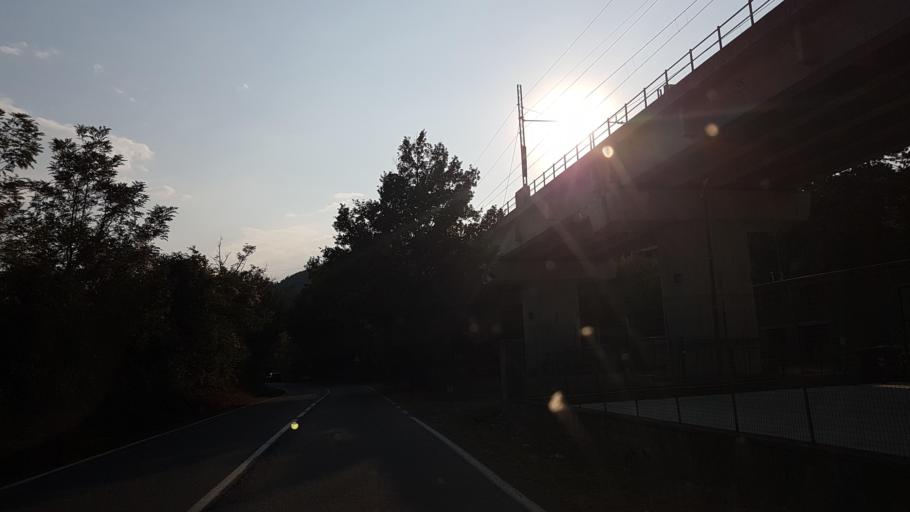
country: IT
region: Emilia-Romagna
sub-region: Provincia di Parma
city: Stazione Valmozzola
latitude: 44.5920
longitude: 9.9511
